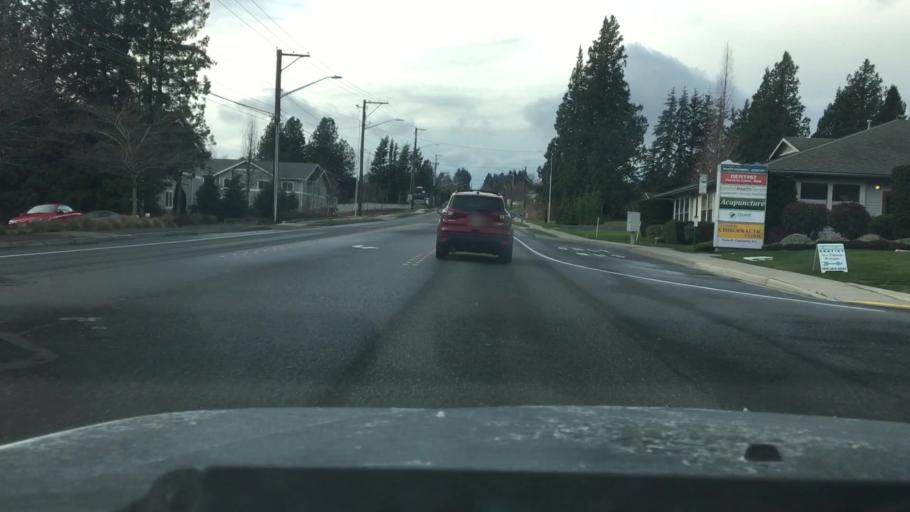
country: US
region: Washington
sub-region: Whatcom County
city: Ferndale
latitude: 48.8484
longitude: -122.6102
